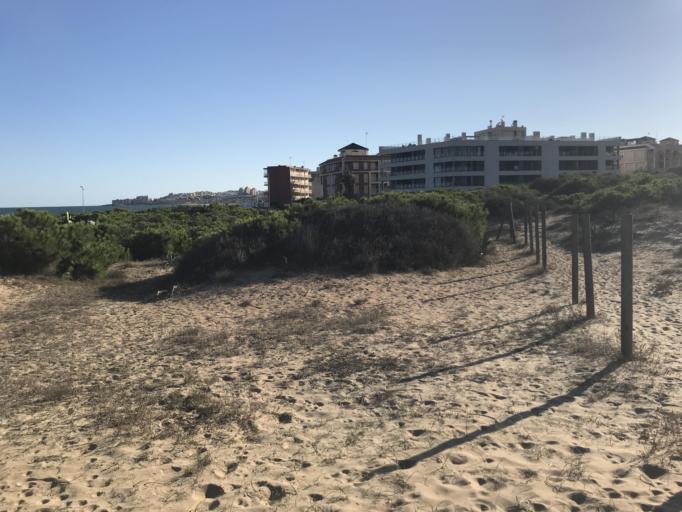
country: ES
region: Valencia
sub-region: Provincia de Alicante
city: Guardamar del Segura
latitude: 38.0308
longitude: -0.6517
